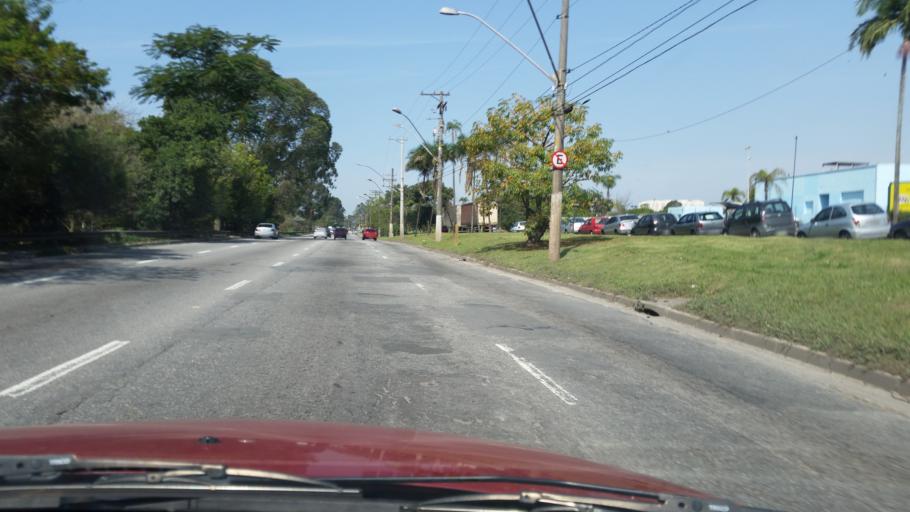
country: BR
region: Sao Paulo
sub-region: Santo Andre
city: Santo Andre
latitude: -23.6550
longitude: -46.5055
